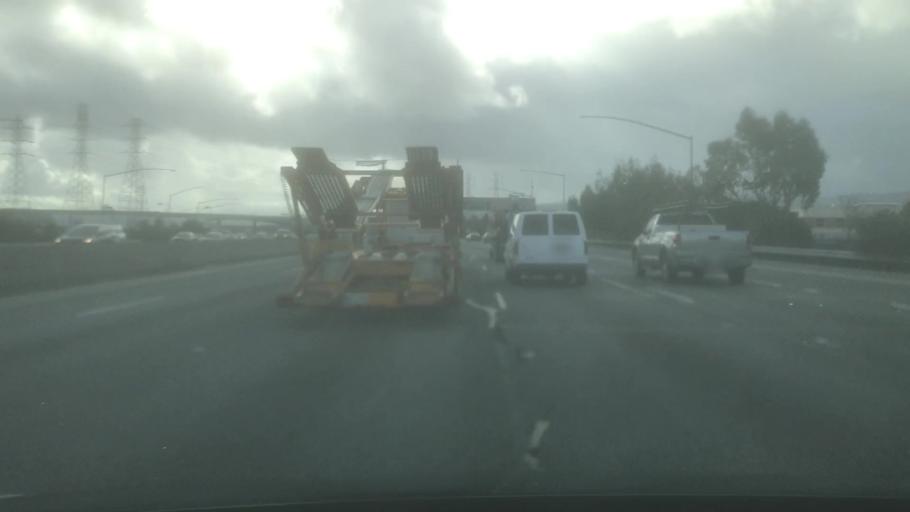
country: US
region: California
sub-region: San Mateo County
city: South San Francisco
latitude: 37.6425
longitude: -122.4064
